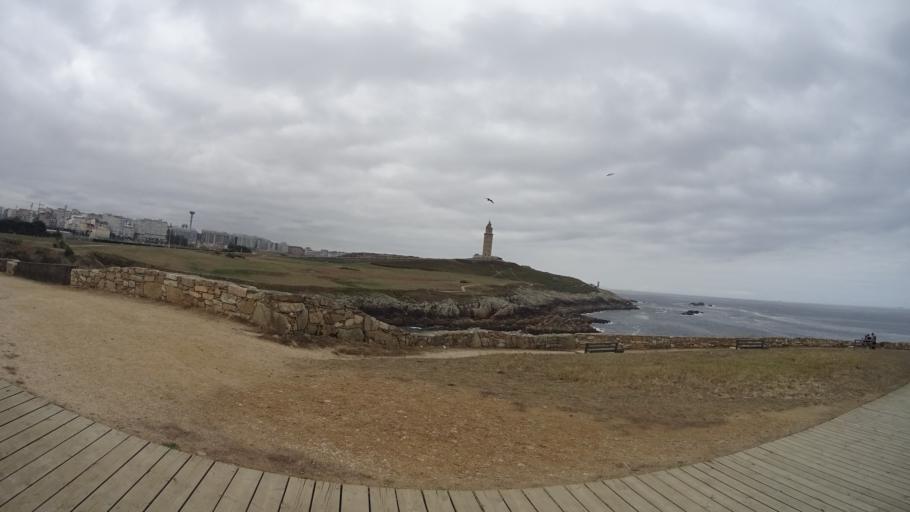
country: ES
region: Galicia
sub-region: Provincia da Coruna
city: A Coruna
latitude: 43.3882
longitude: -8.3998
